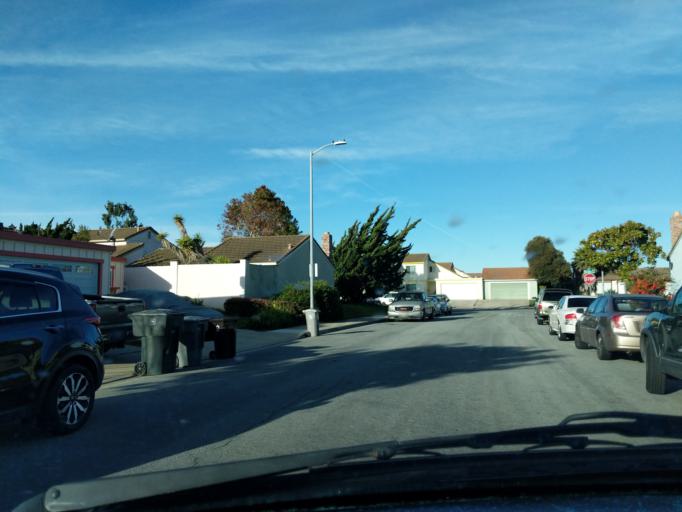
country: US
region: California
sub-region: Monterey County
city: Boronda
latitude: 36.7081
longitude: -121.6593
